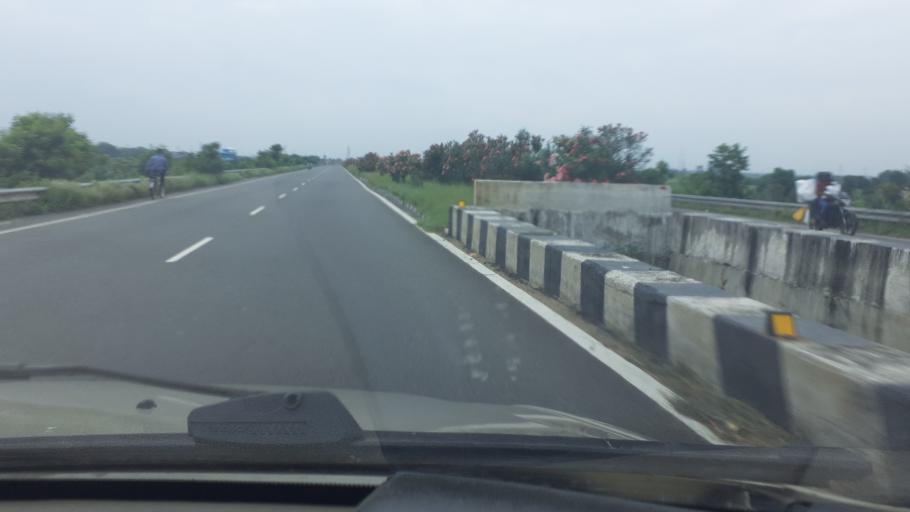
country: IN
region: Tamil Nadu
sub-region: Madurai
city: Tirupparangunram
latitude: 9.8357
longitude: 77.9964
